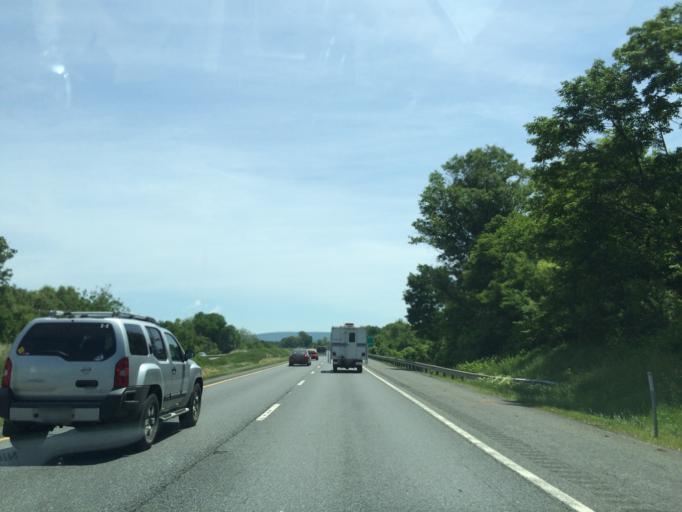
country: US
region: Maryland
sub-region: Washington County
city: Hagerstown
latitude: 39.6019
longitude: -77.7100
